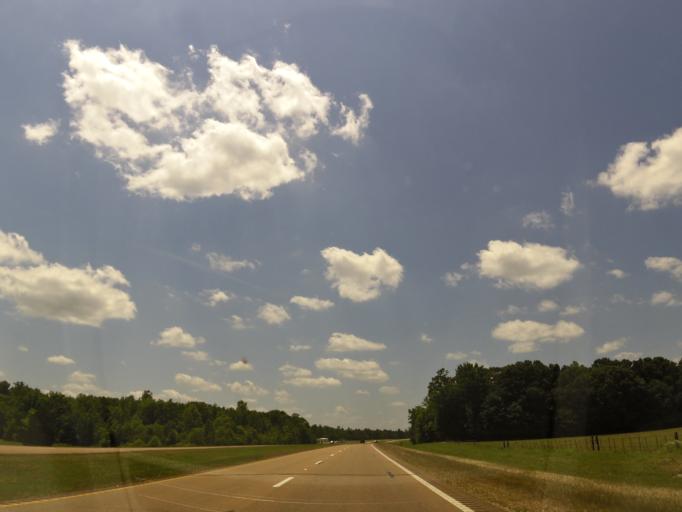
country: US
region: Mississippi
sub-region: Pontotoc County
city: Pontotoc
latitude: 34.2815
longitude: -89.1168
